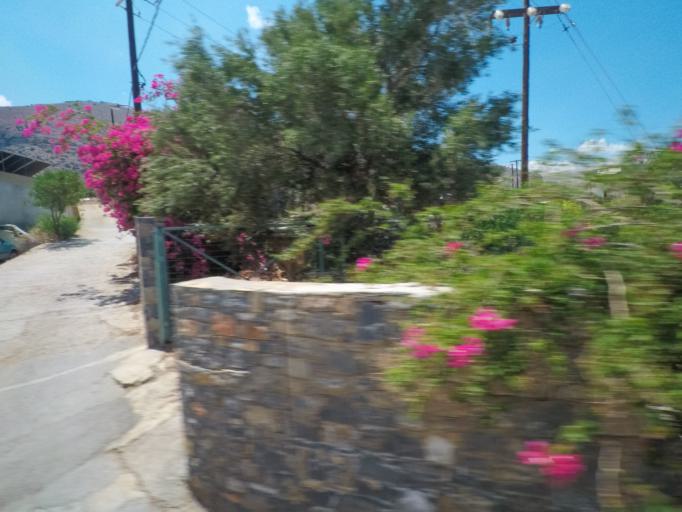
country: GR
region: Crete
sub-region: Nomos Lasithiou
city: Skhisma
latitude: 35.2452
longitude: 25.7298
